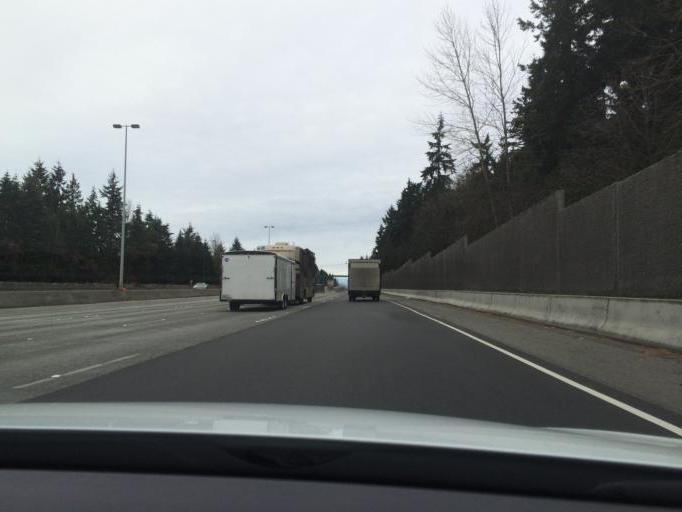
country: US
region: Washington
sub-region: King County
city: Yarrow Point
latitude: 47.6402
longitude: -122.1863
